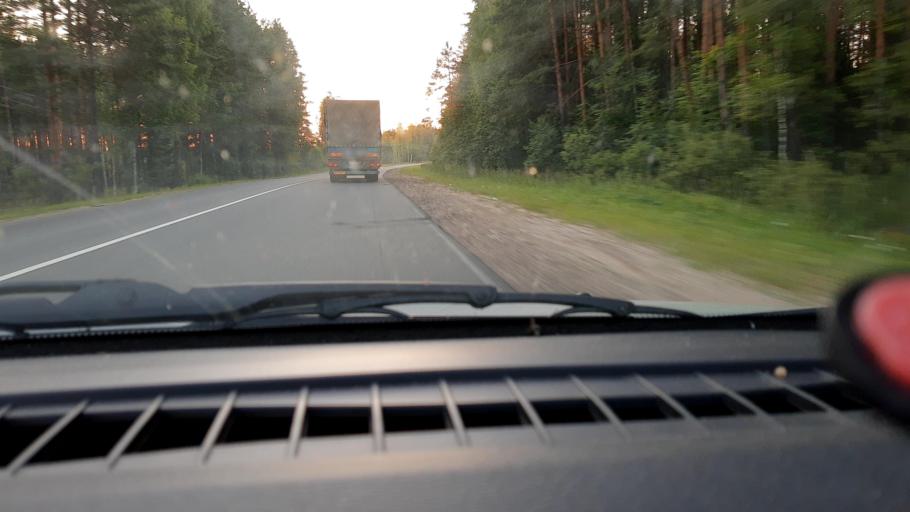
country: RU
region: Nizjnij Novgorod
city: Uren'
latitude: 57.3682
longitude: 45.6940
